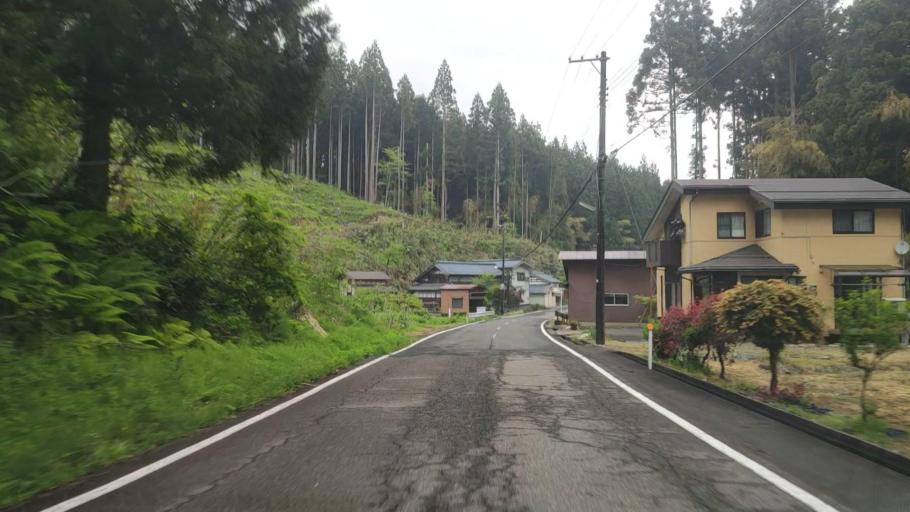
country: JP
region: Niigata
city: Gosen
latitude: 37.7205
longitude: 139.1272
